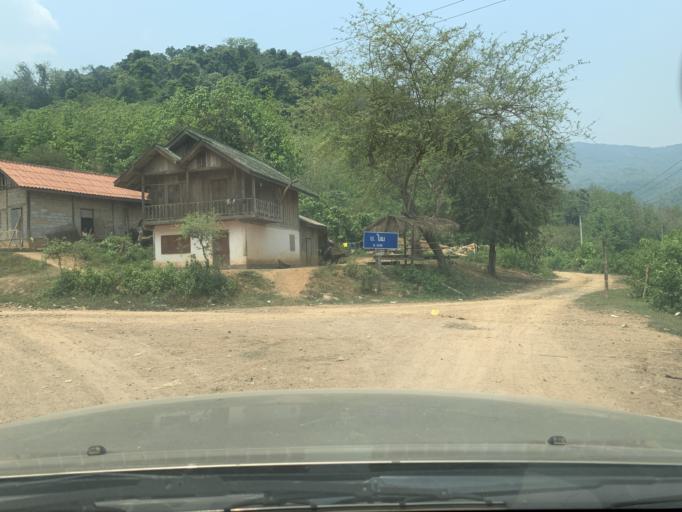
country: LA
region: Louangphabang
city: Louangphabang
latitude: 19.9701
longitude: 102.1250
